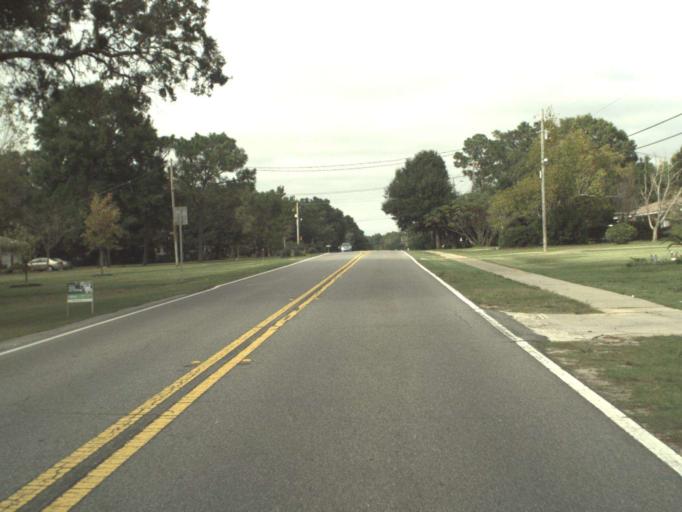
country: US
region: Florida
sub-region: Escambia County
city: East Pensacola Heights
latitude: 30.4381
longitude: -87.1822
